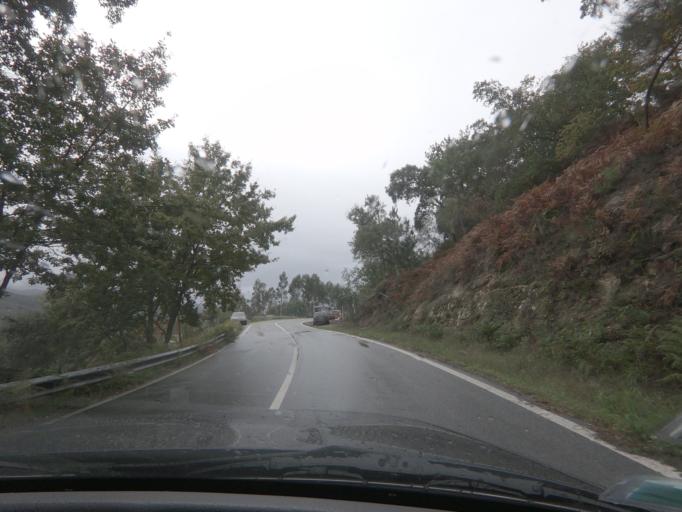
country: PT
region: Vila Real
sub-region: Mondim de Basto
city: Mondim de Basto
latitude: 41.3712
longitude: -7.9295
